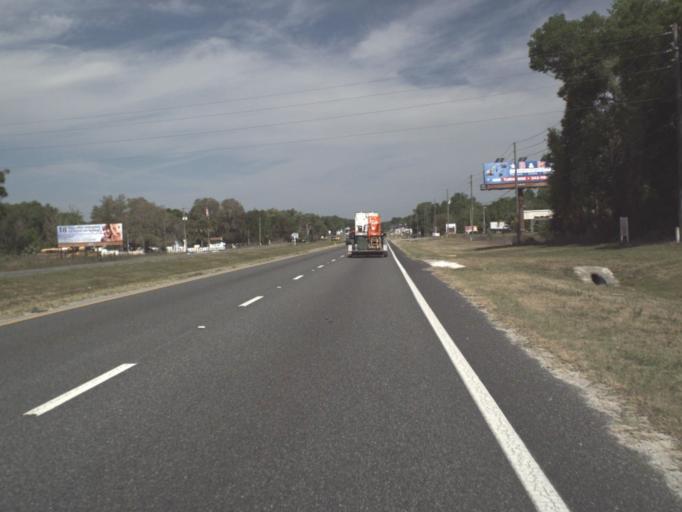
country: US
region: Florida
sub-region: Marion County
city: Belleview
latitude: 29.0364
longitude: -82.0270
